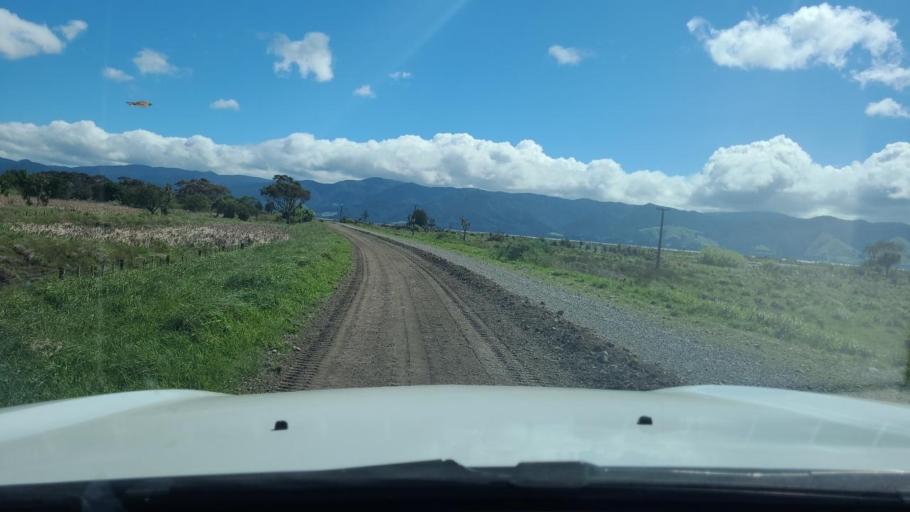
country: NZ
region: Wellington
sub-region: Upper Hutt City
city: Upper Hutt
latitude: -41.2426
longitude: 175.2709
